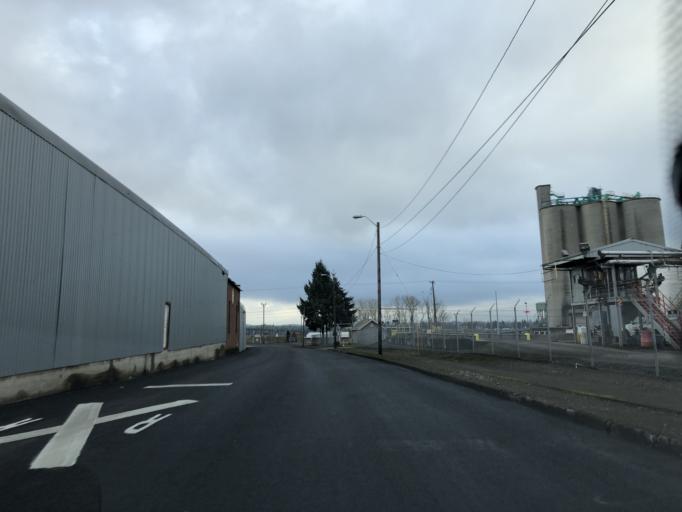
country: US
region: Washington
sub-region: Clark County
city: Vancouver
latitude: 45.6286
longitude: -122.6860
